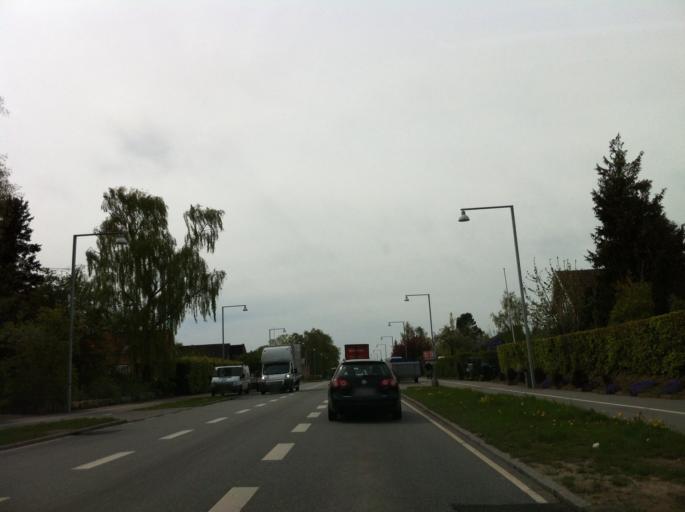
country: DK
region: Zealand
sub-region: Lejre Kommune
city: Osted
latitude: 55.5521
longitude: 11.9497
